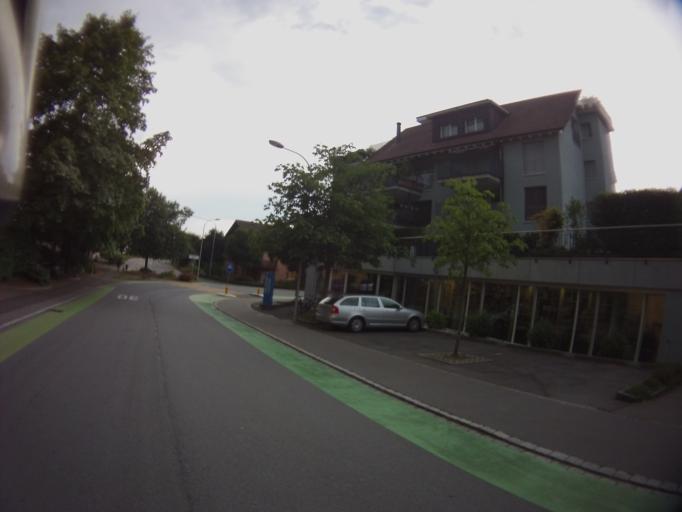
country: CH
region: Zug
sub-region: Zug
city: Hunenberg
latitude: 47.1753
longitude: 8.4259
